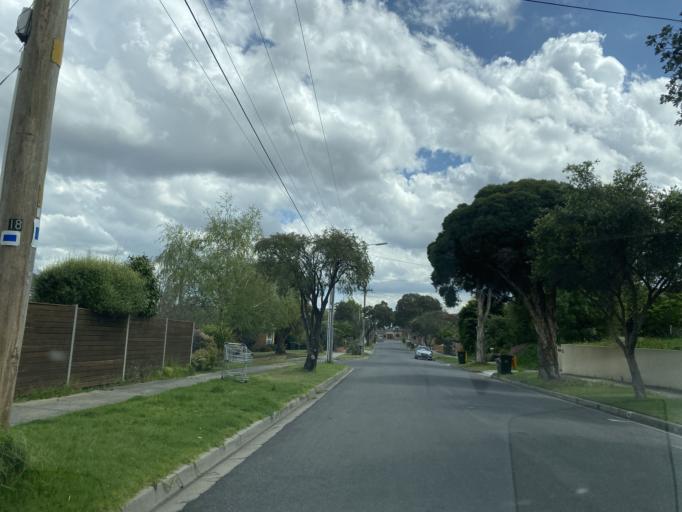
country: AU
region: Victoria
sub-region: Whitehorse
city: Burwood
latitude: -37.8546
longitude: 145.1259
